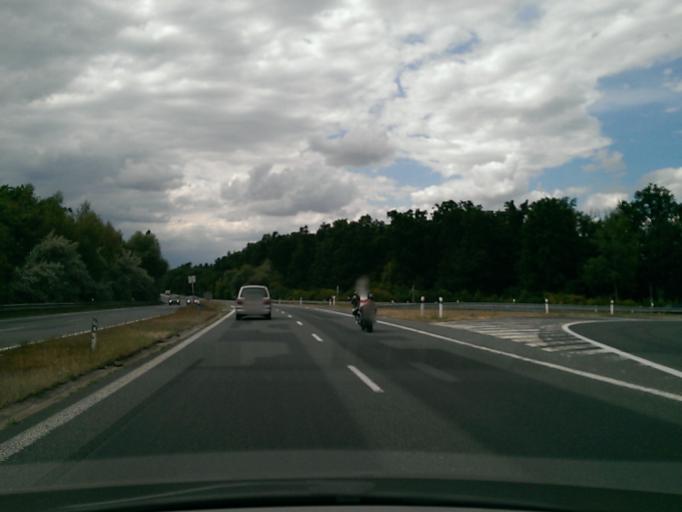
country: CZ
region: Central Bohemia
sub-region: Okres Nymburk
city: Podebrady
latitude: 50.1190
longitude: 15.1237
